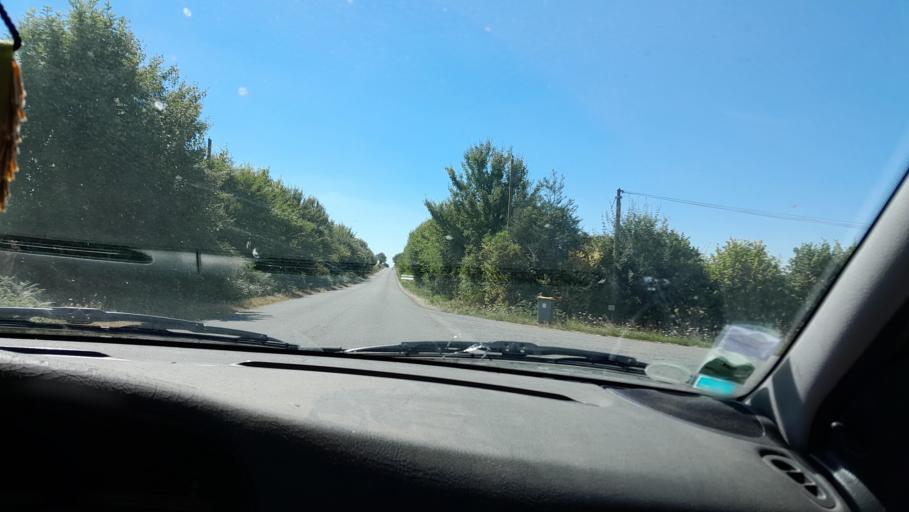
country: FR
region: Pays de la Loire
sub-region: Departement de la Mayenne
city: Congrier
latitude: 47.8363
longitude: -1.1568
